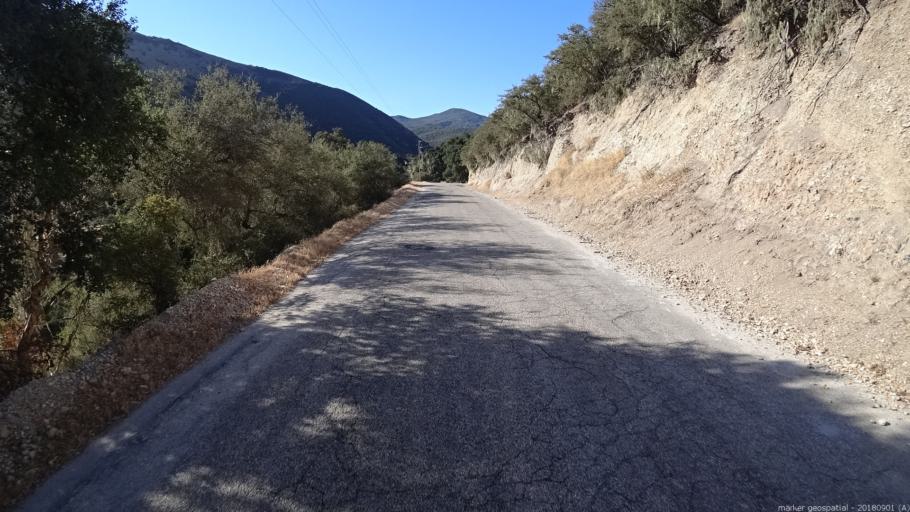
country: US
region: California
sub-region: Monterey County
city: Greenfield
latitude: 36.2019
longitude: -121.2764
